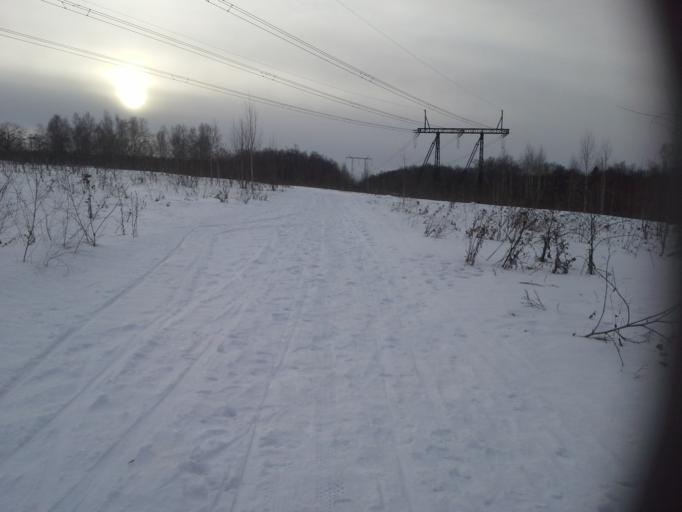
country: RU
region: Moscow
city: Yasenevo
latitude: 55.5745
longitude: 37.5449
